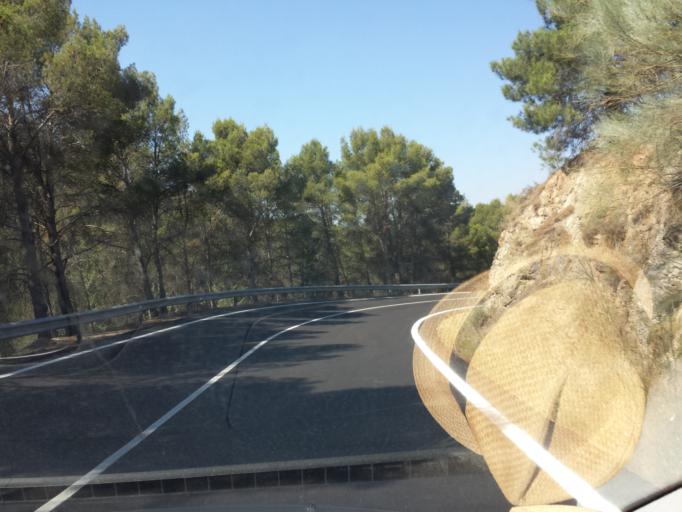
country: ES
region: Aragon
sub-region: Provincia de Zaragoza
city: Munebrega
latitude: 41.2229
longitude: -1.7423
